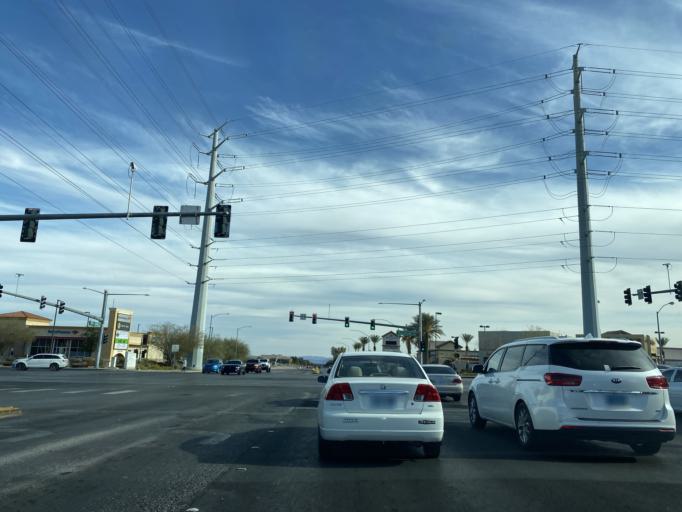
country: US
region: Nevada
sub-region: Clark County
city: Enterprise
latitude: 36.0557
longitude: -115.2436
